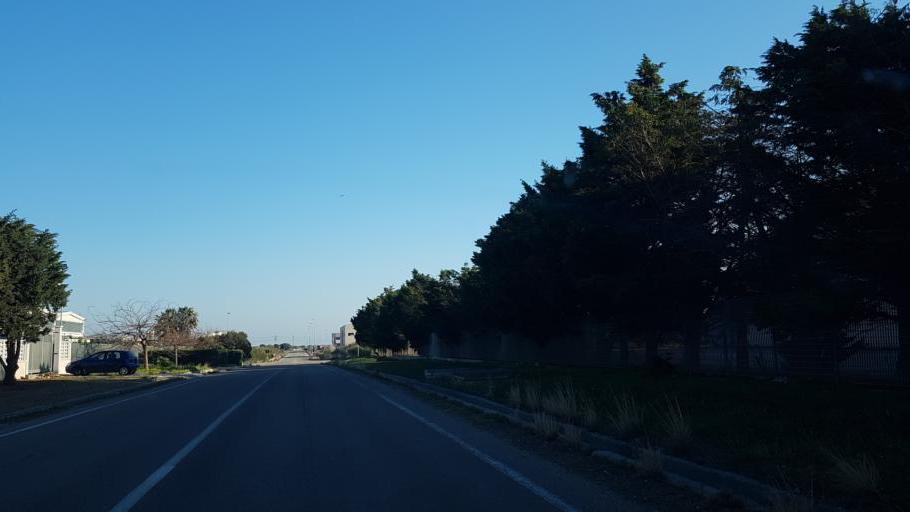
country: IT
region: Apulia
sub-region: Provincia di Brindisi
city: La Rosa
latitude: 40.6270
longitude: 17.9693
